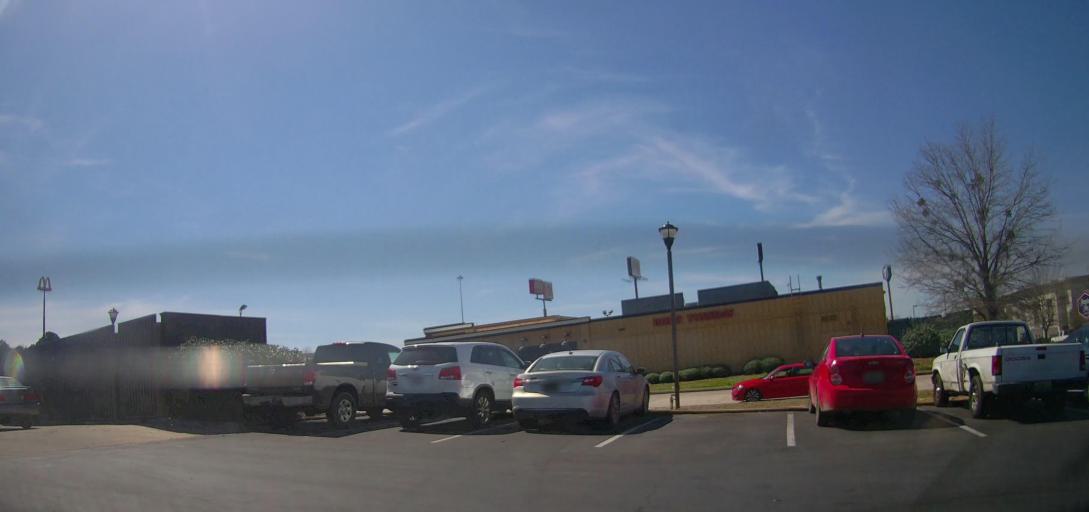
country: US
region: Alabama
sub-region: Cullman County
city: Cullman
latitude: 34.2082
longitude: -86.8762
